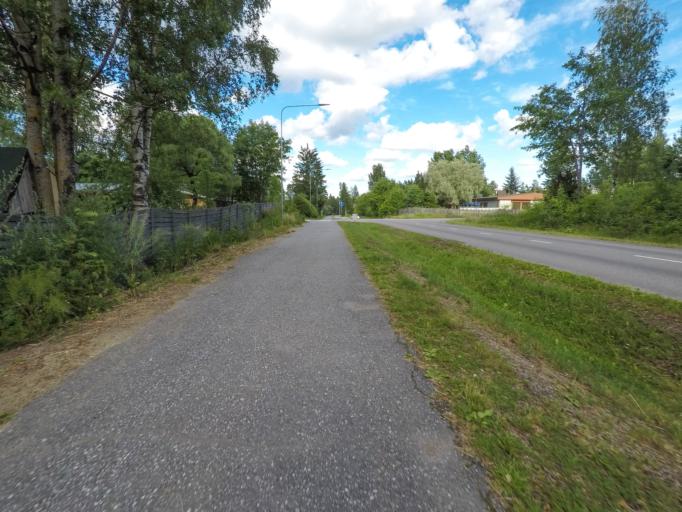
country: FI
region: South Karelia
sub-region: Lappeenranta
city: Joutseno
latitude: 61.1217
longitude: 28.4772
